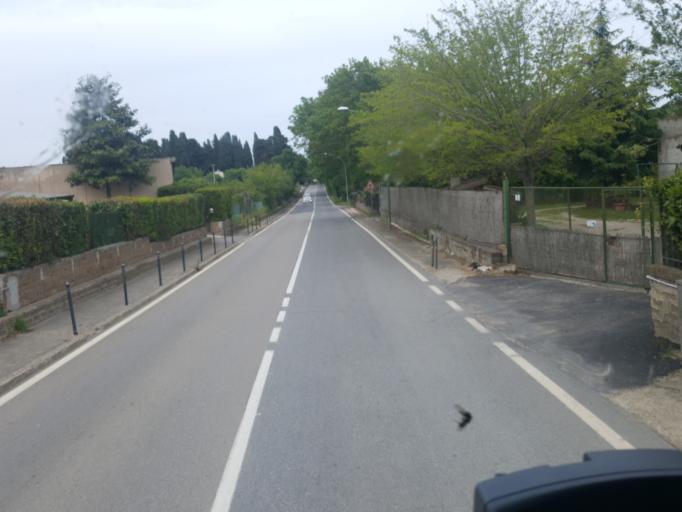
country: IT
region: Latium
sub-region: Provincia di Viterbo
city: Monte Romano
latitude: 42.2716
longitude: 11.9049
